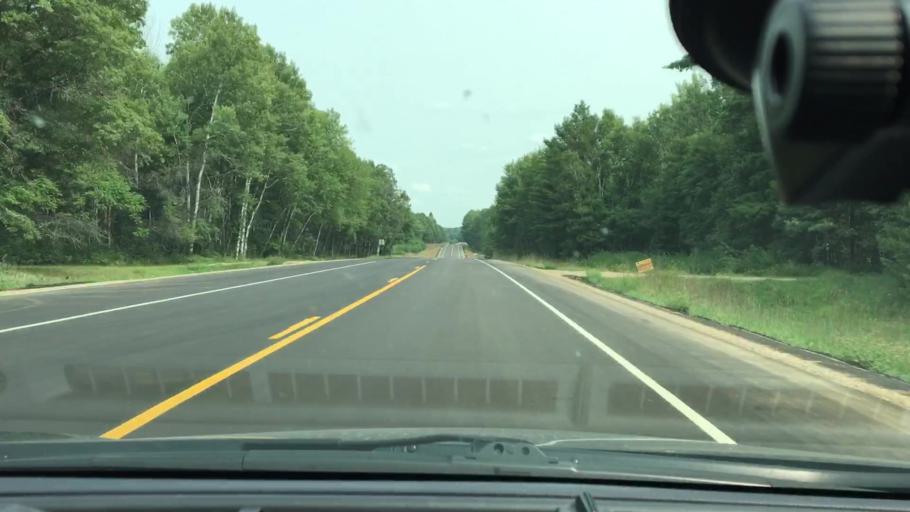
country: US
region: Minnesota
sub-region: Crow Wing County
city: Nisswa
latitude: 46.5294
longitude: -94.2457
